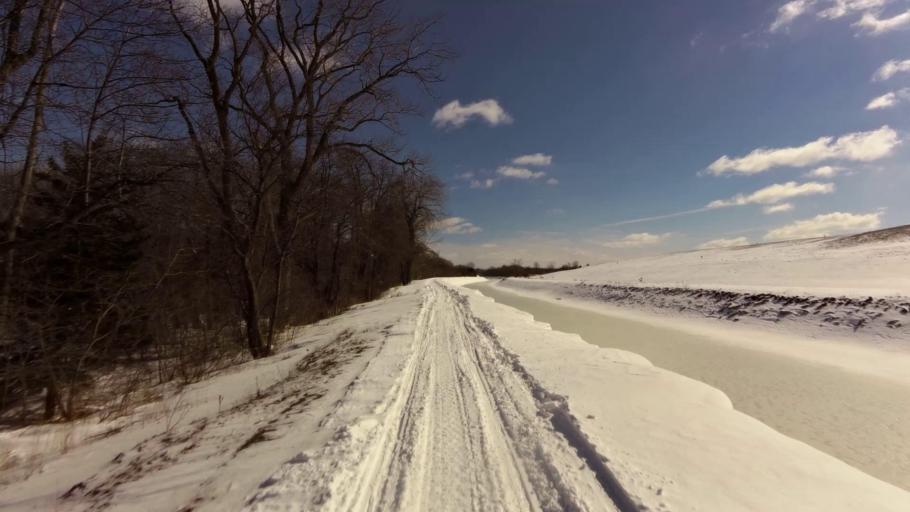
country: US
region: New York
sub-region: Orleans County
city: Albion
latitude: 43.2514
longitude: -78.1241
